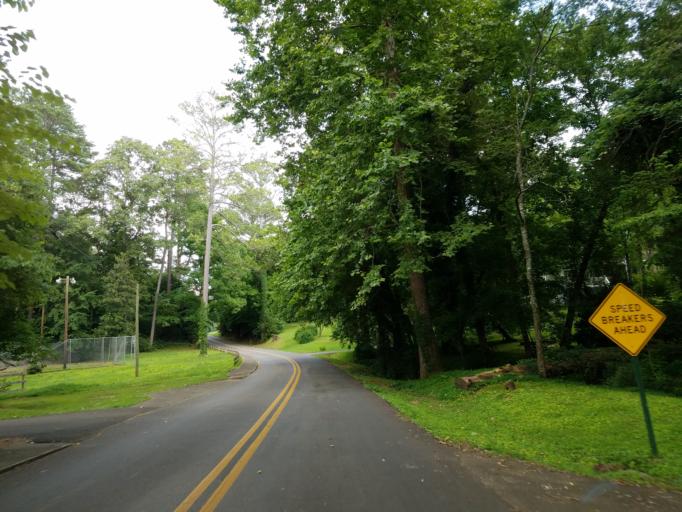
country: US
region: Georgia
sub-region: Pickens County
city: Nelson
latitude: 34.4188
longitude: -84.3847
